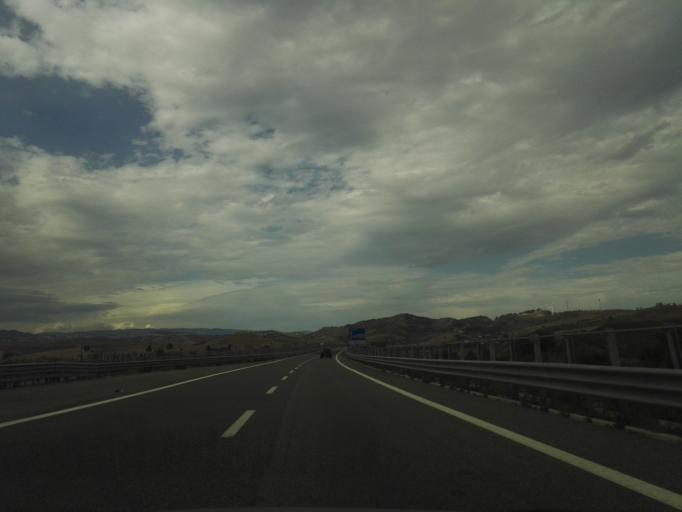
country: IT
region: Calabria
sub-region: Provincia di Catanzaro
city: Roccelletta
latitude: 38.8461
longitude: 16.5722
